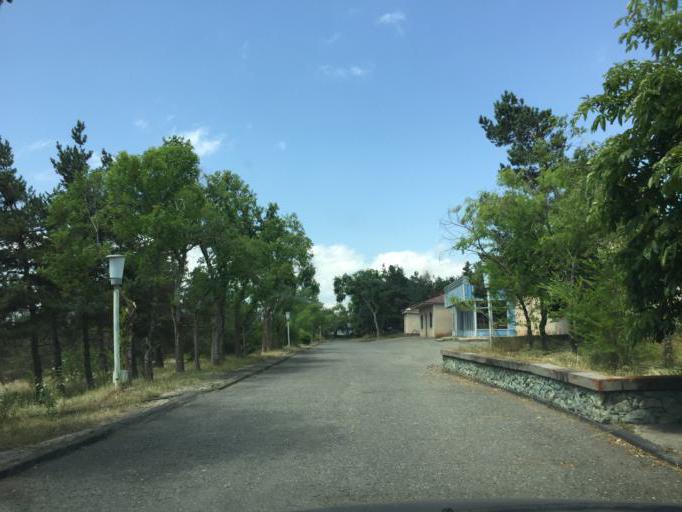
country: AM
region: Geghark'unik'i Marz
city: Tsovagyugh
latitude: 40.6219
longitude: 45.0167
